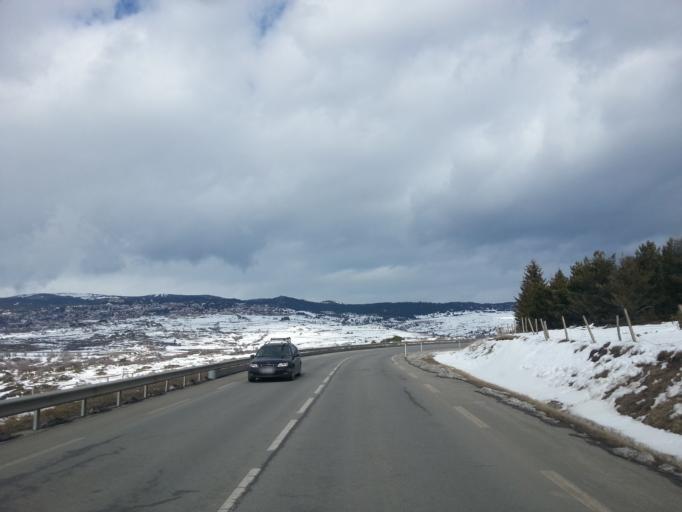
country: ES
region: Catalonia
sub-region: Provincia de Girona
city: Llivia
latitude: 42.4755
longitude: 2.0547
